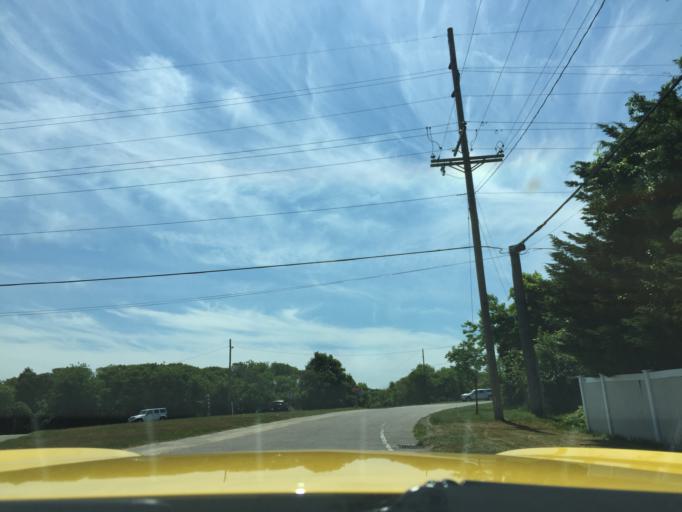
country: US
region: New York
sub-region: Suffolk County
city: Montauk
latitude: 41.0432
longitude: -71.9272
